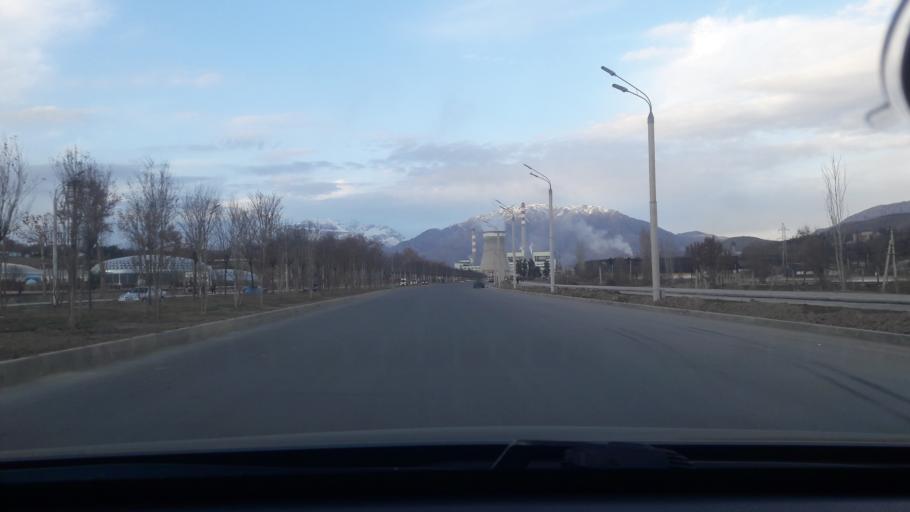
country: TJ
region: Dushanbe
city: Dushanbe
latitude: 38.5963
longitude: 68.7766
